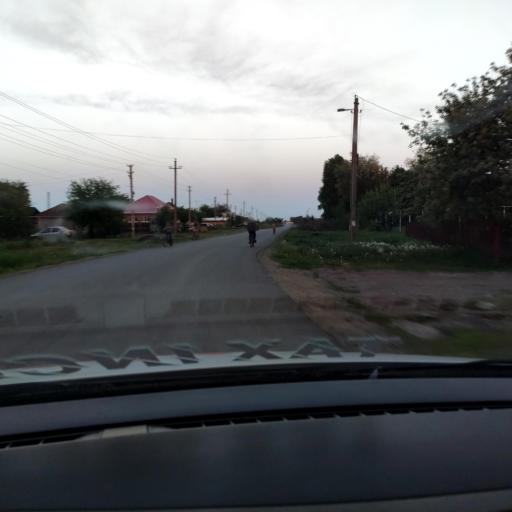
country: RU
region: Voronezj
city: Novovoronezh
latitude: 51.4127
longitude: 39.3064
